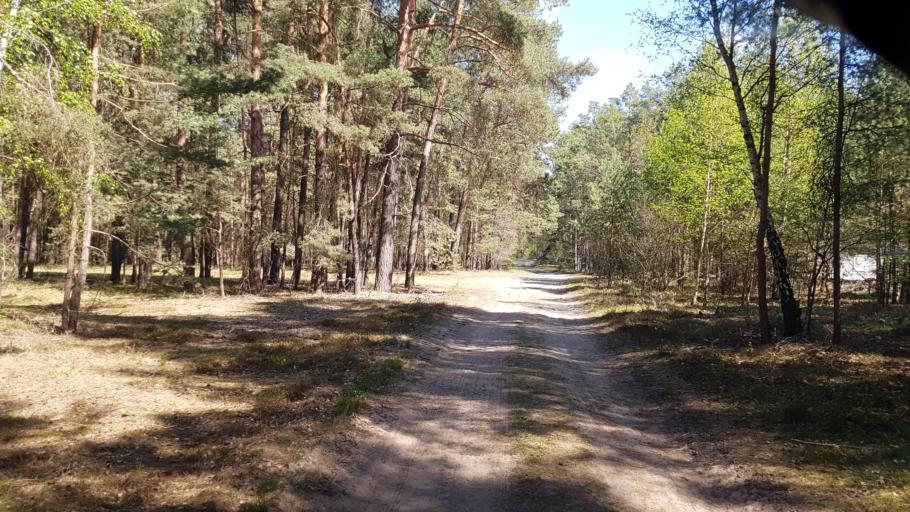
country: DE
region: Brandenburg
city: Crinitz
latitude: 51.7474
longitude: 13.7637
